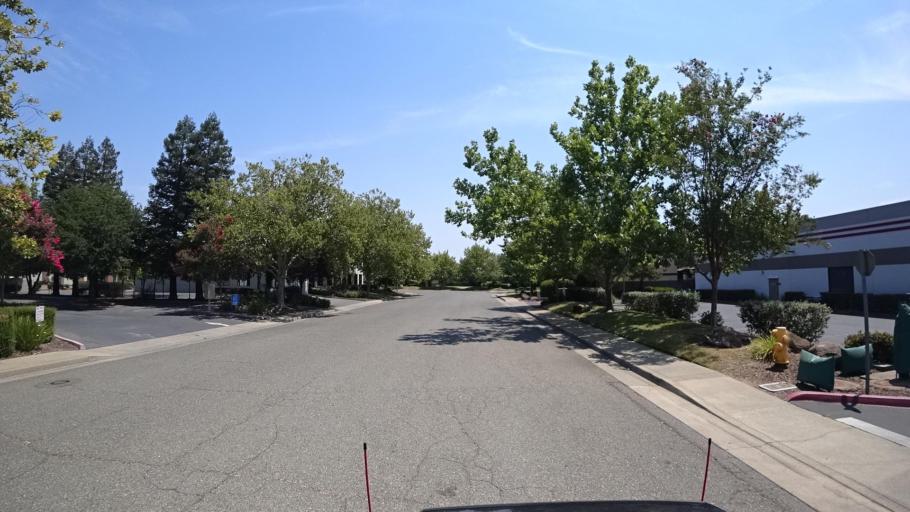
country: US
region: California
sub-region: Placer County
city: Rocklin
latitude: 38.8074
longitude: -121.2172
